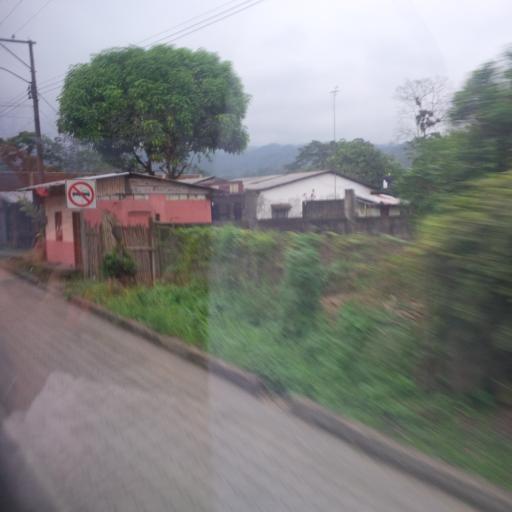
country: EC
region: Chimborazo
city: Alausi
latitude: -2.1990
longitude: -79.1167
